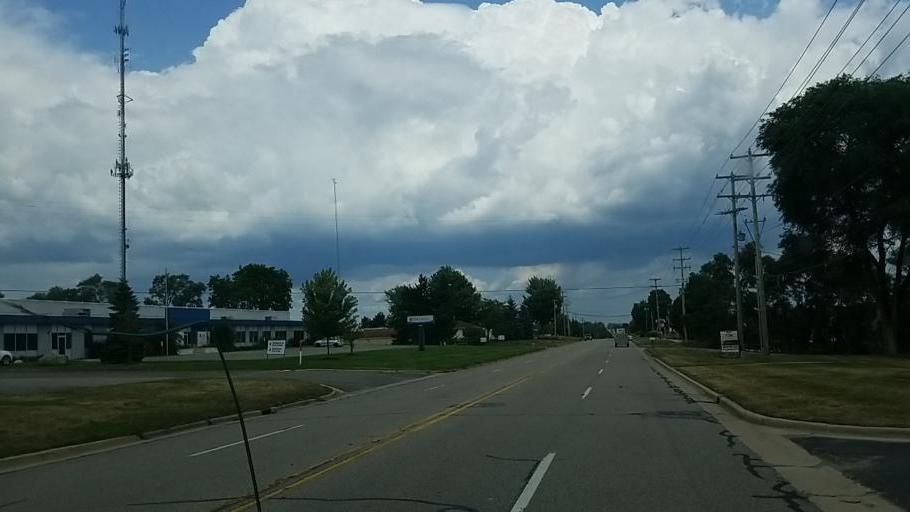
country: US
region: Michigan
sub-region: Kent County
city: Walker
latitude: 43.0153
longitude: -85.7423
